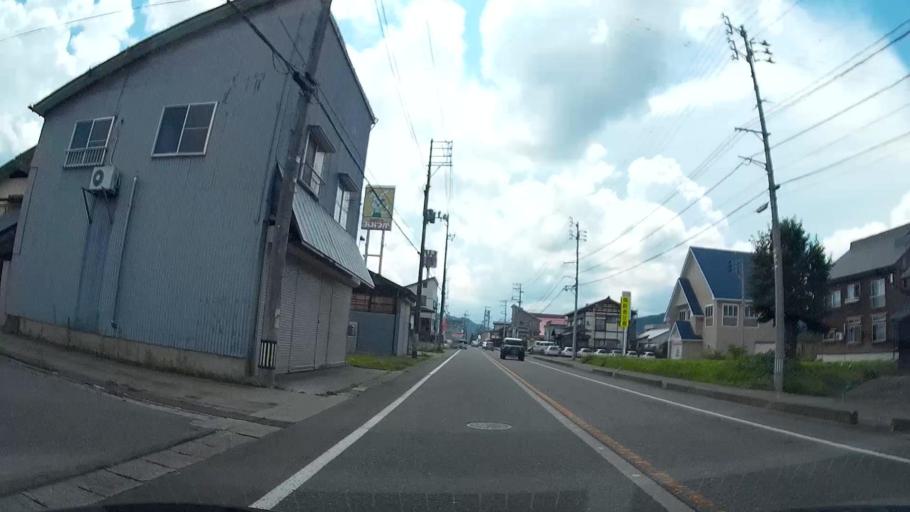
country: JP
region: Niigata
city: Tokamachi
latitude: 37.0209
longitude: 138.6572
